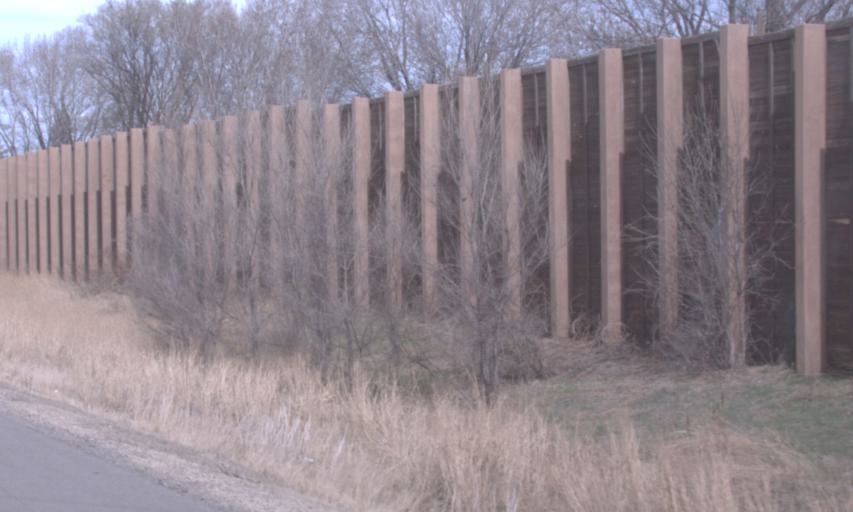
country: US
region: Minnesota
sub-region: Anoka County
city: Coon Rapids
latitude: 45.1678
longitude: -93.2910
